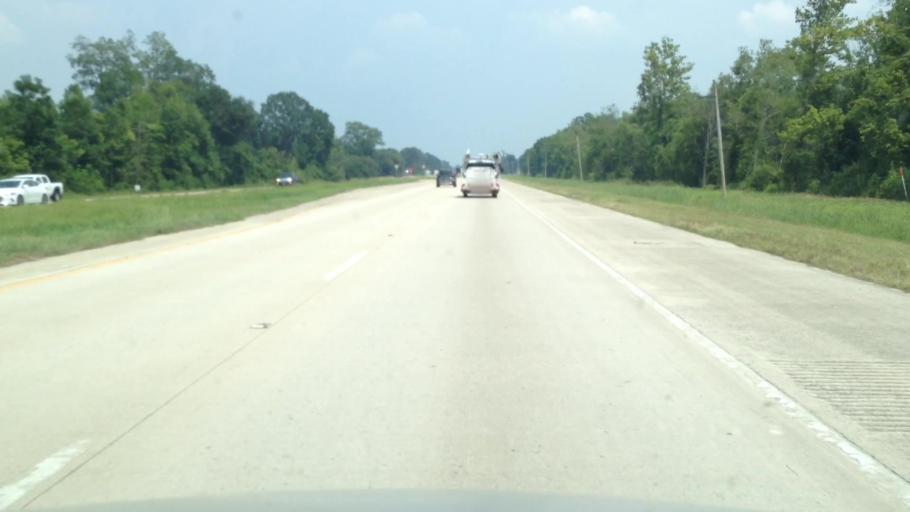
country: US
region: Louisiana
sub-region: West Baton Rouge Parish
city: Erwinville
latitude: 30.5055
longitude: -91.3259
